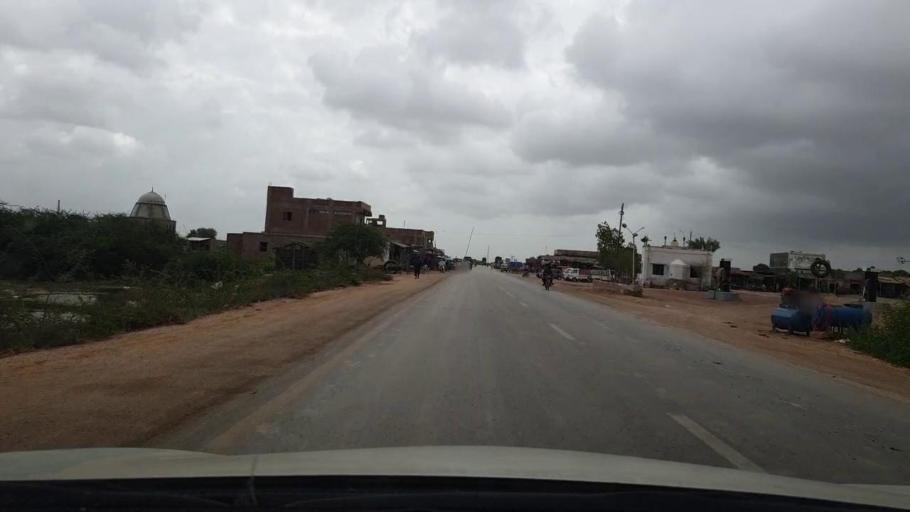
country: PK
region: Sindh
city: Mirpur Batoro
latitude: 24.6438
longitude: 68.4112
